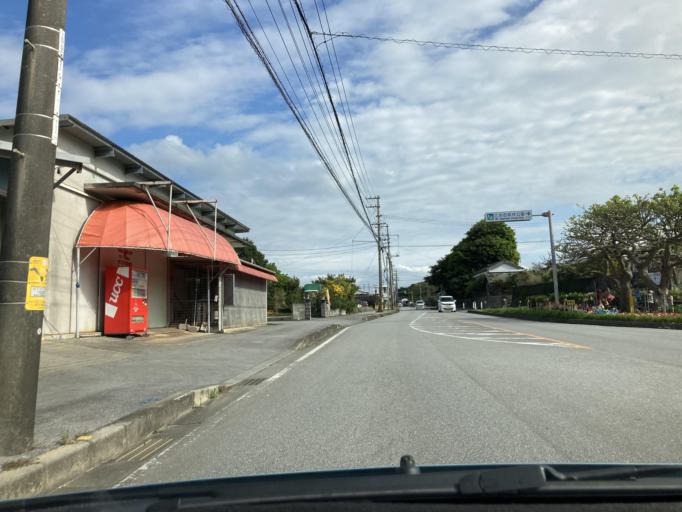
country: JP
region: Okinawa
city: Nago
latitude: 26.6923
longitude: 127.9579
